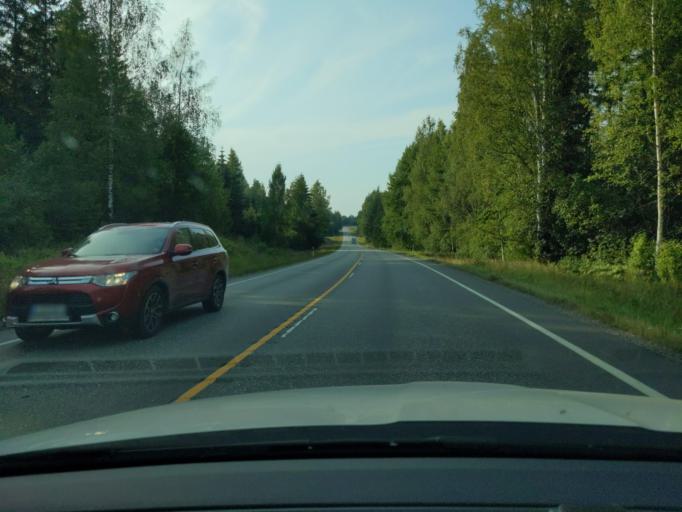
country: FI
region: Paijanne Tavastia
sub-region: Lahti
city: Padasjoki
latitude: 61.3344
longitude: 25.2671
